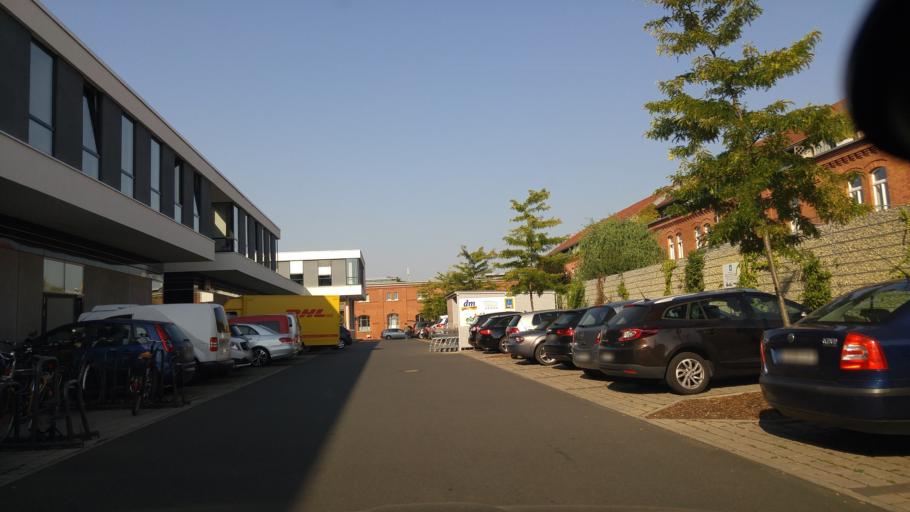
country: DE
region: Bavaria
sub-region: Regierungsbezirk Mittelfranken
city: Erlangen
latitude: 49.5926
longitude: 11.0282
